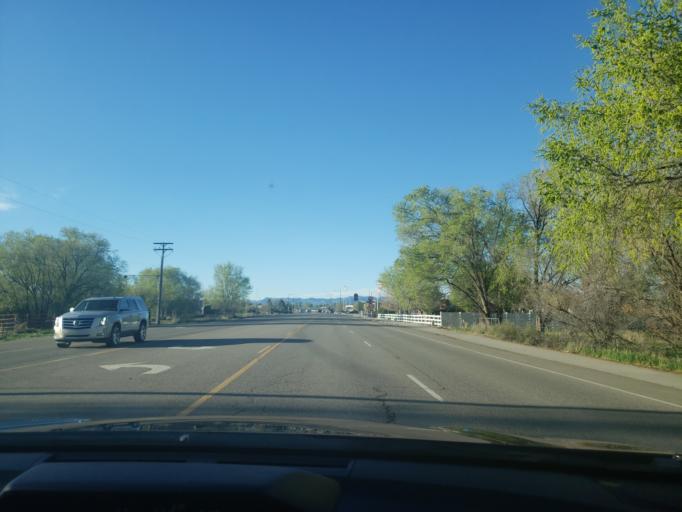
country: US
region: Colorado
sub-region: Mesa County
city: Fruita
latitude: 39.1484
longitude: -108.7382
